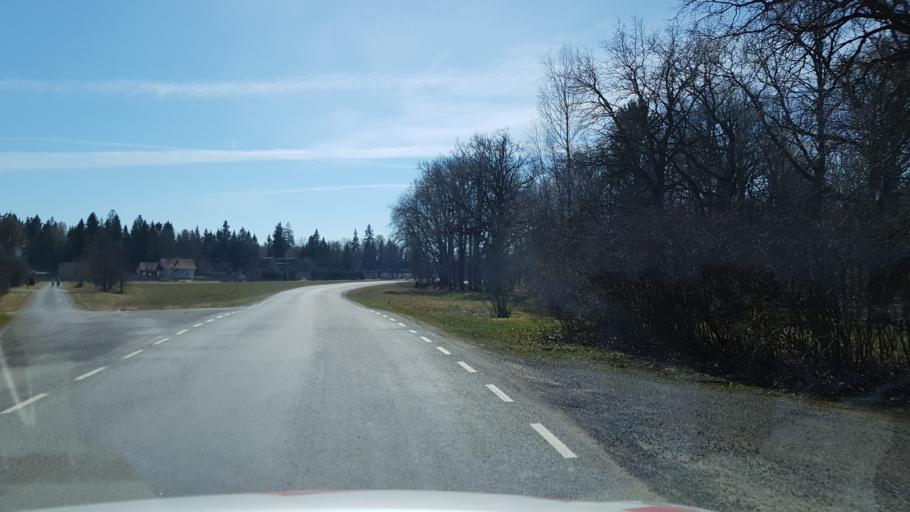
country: EE
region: Laeaene-Virumaa
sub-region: Vinni vald
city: Vinni
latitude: 59.2880
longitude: 26.4268
